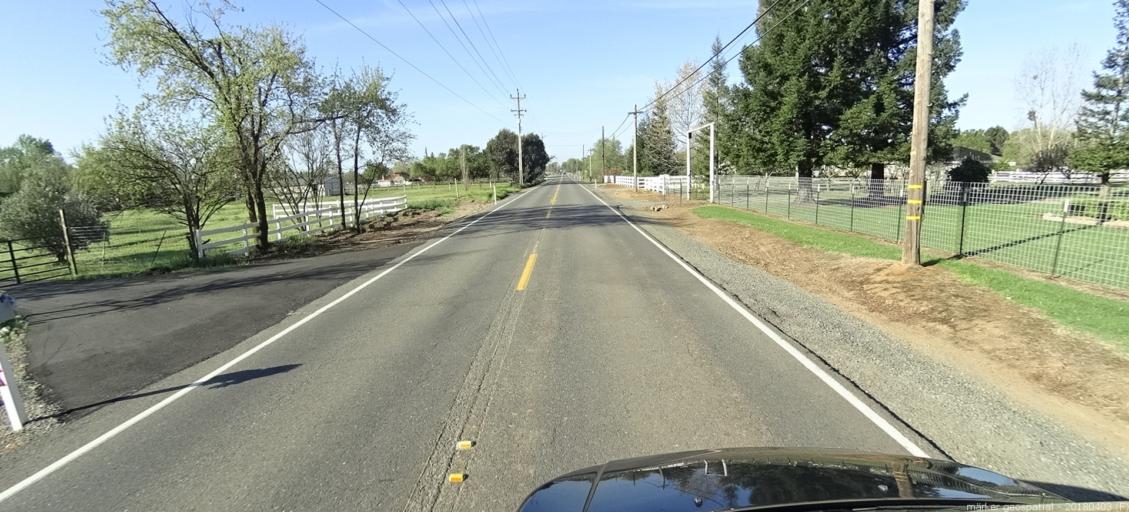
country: US
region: California
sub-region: Sacramento County
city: Wilton
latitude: 38.4380
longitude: -121.1944
